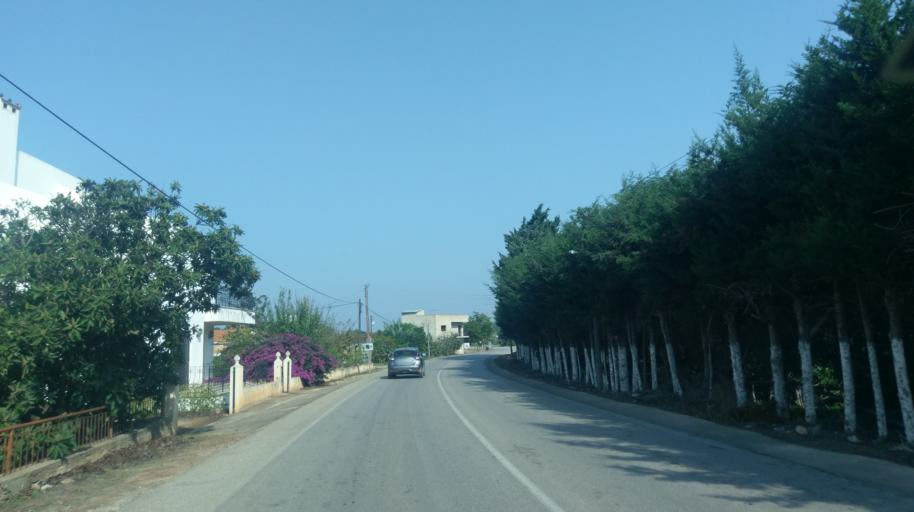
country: CY
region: Ammochostos
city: Leonarisso
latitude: 35.4979
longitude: 34.1588
